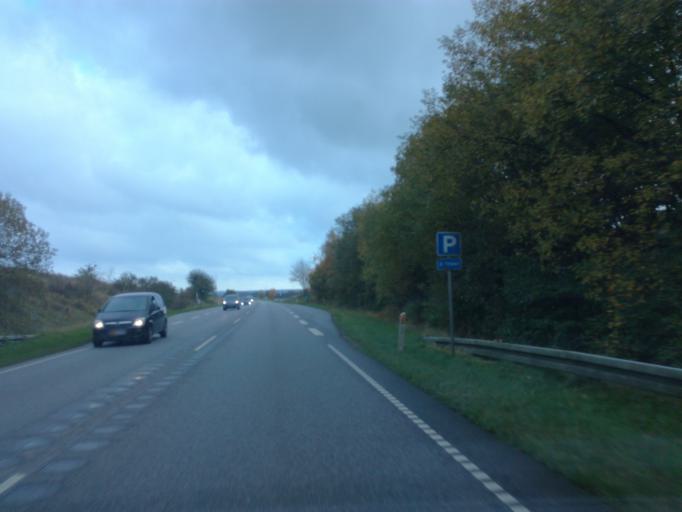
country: DK
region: South Denmark
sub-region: Vejle Kommune
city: Brejning
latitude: 55.6300
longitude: 9.6985
